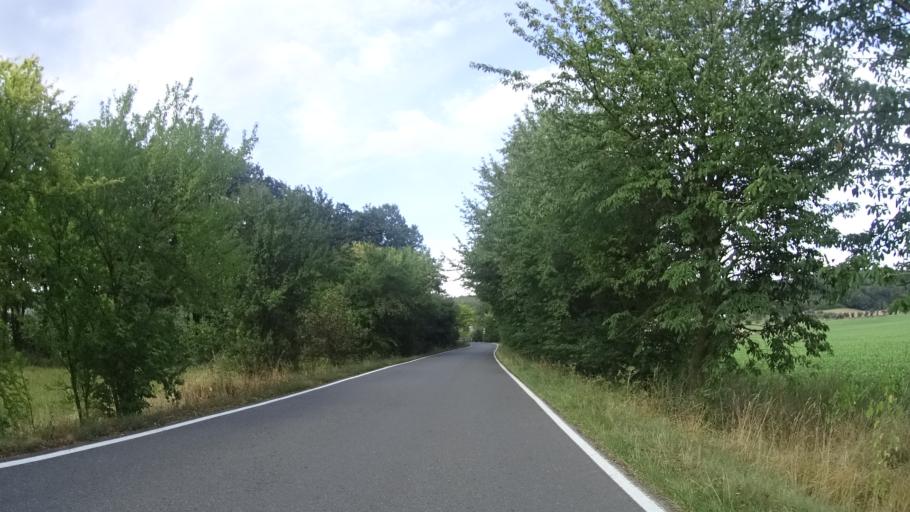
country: CZ
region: Olomoucky
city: Dubicko
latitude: 49.8420
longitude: 16.9437
